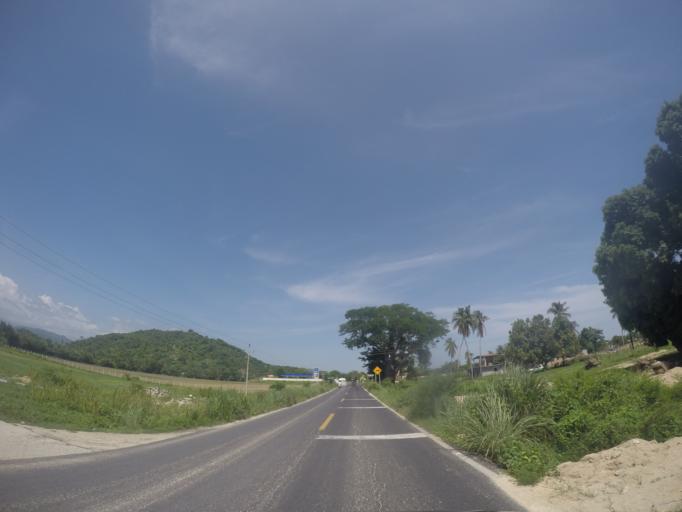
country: MX
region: Oaxaca
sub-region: Villa de Tututepec de Melchor Ocampo
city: Santa Rosa de Lima
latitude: 16.0110
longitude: -97.4539
